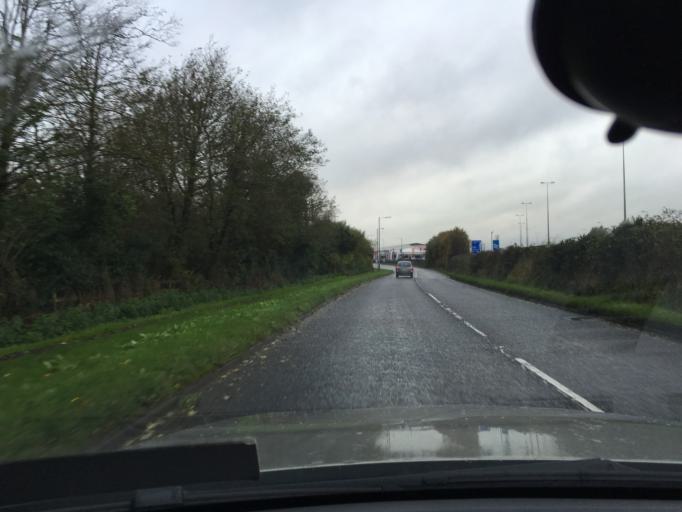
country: GB
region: Northern Ireland
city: Carnmoney
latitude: 54.6706
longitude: -5.9702
